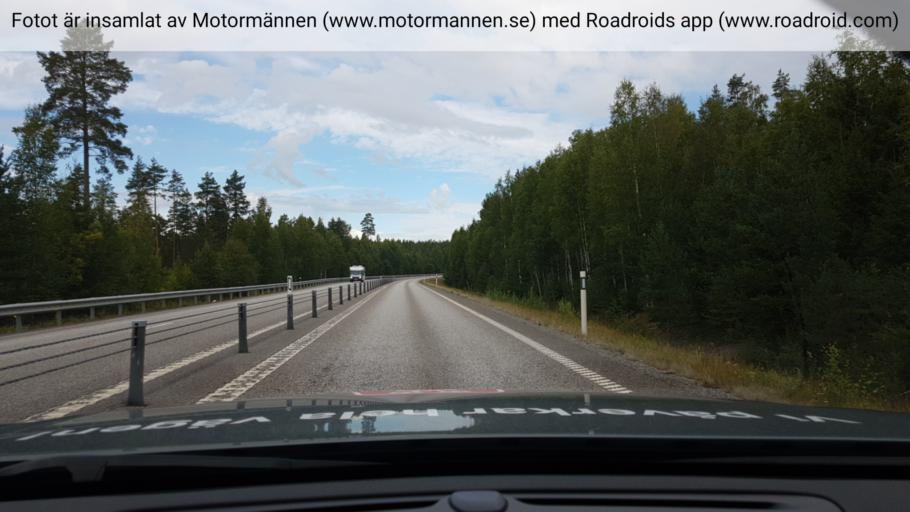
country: SE
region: Uppsala
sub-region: Heby Kommun
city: Tarnsjo
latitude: 60.1784
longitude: 16.9480
